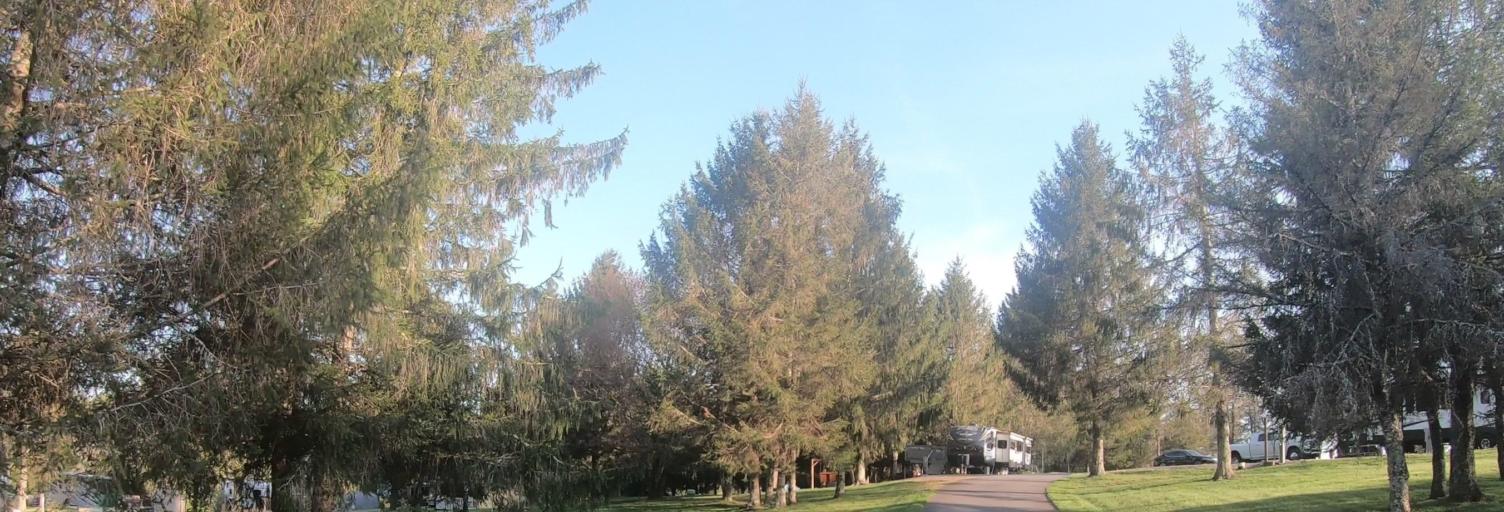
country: US
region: North Carolina
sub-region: Ashe County
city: Jefferson
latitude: 36.3547
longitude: -81.3777
